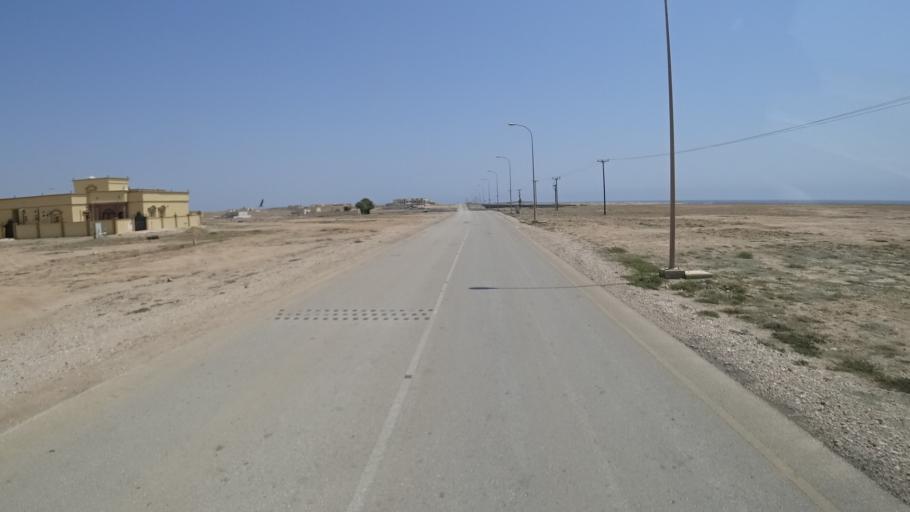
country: OM
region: Zufar
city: Salalah
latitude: 16.9789
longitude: 54.7096
